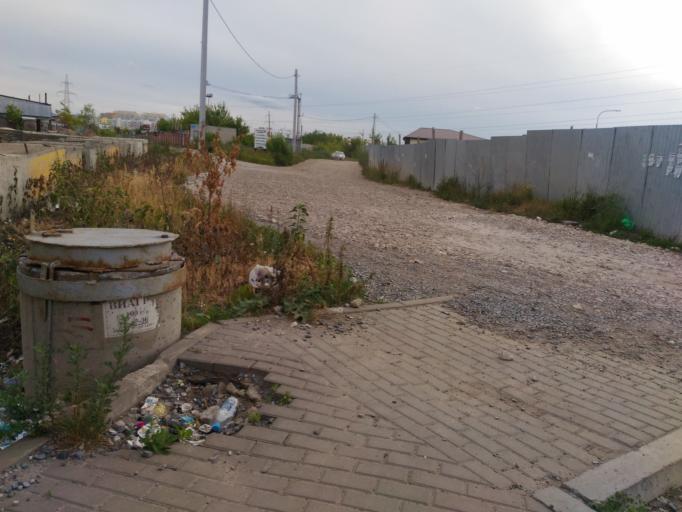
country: RU
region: Ulyanovsk
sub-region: Ulyanovskiy Rayon
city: Ulyanovsk
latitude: 54.2854
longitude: 48.2832
